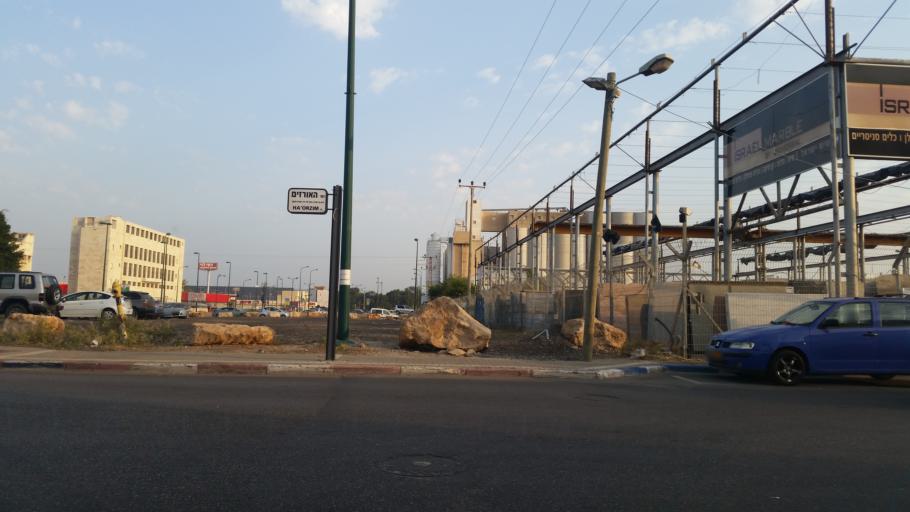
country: IL
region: Central District
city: Netanya
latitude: 32.3180
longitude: 34.8720
